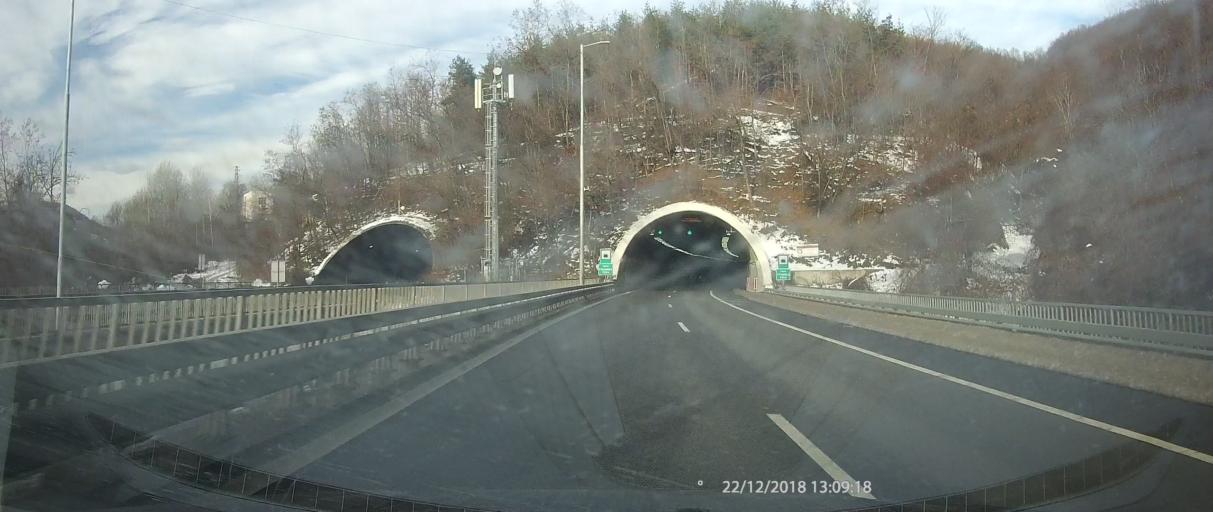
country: BG
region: Sofiya
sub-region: Obshtina Botevgrad
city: Botevgrad
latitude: 42.8527
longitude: 23.7900
